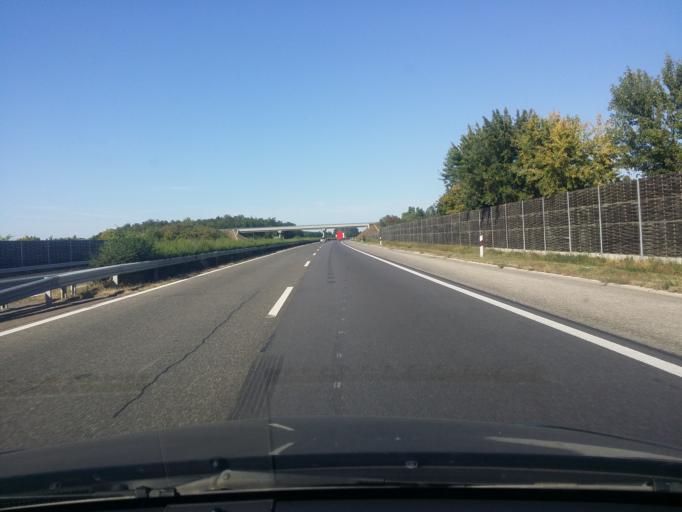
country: HU
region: Bacs-Kiskun
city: Balloszog
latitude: 46.9035
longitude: 19.6170
